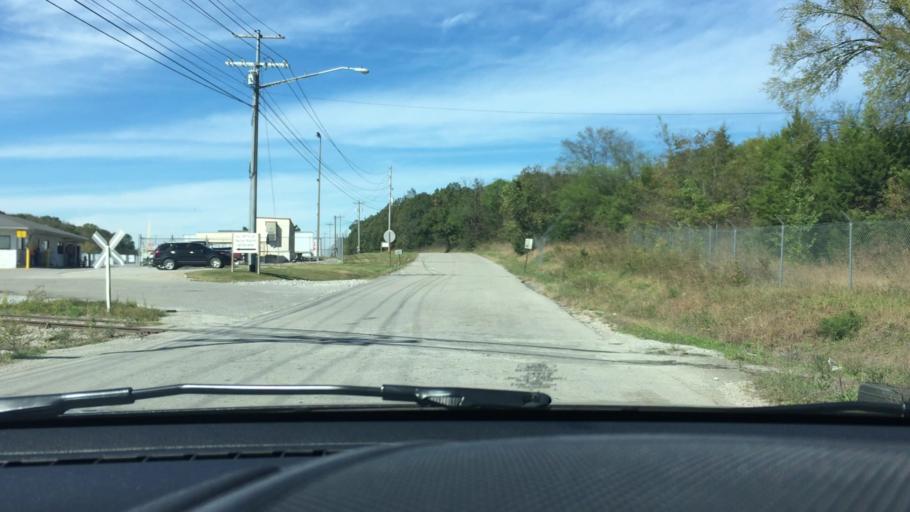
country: US
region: Tennessee
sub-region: Giles County
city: Pulaski
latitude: 35.2175
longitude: -87.0624
